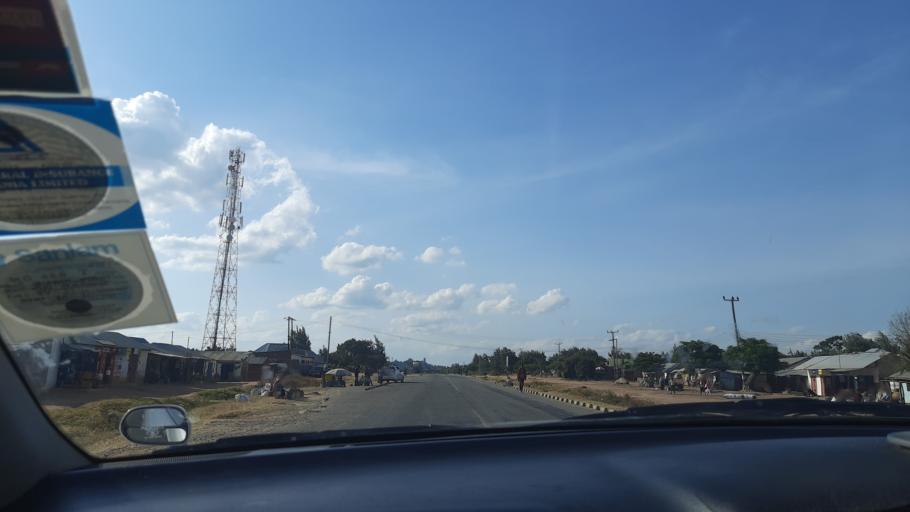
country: TZ
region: Singida
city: Puma
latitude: -5.0043
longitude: 34.7574
